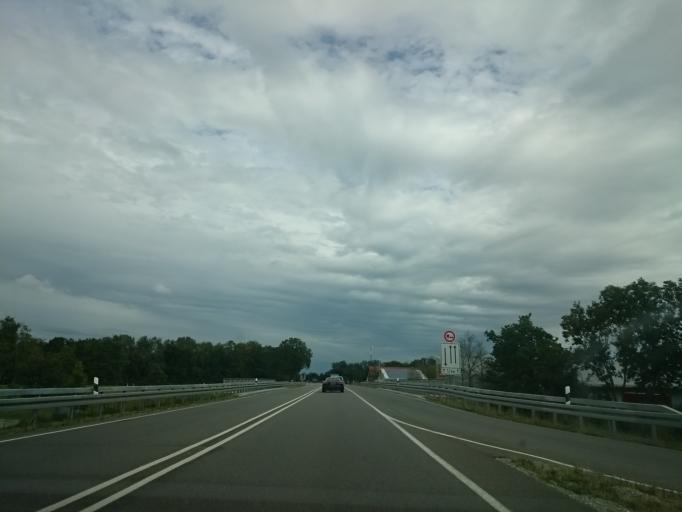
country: DE
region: Bavaria
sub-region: Swabia
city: Jengen
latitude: 48.0032
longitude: 10.7203
